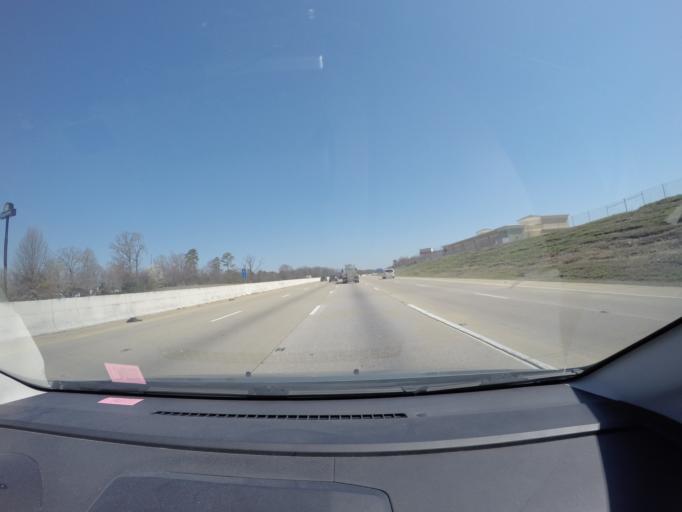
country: US
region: Tennessee
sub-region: Hamilton County
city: East Brainerd
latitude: 35.0448
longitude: -85.1534
